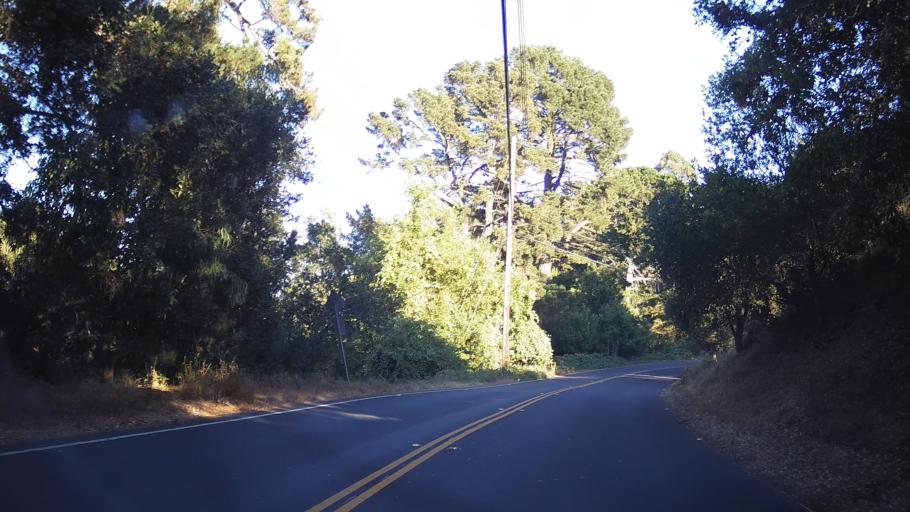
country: US
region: California
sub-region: Contra Costa County
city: Orinda
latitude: 37.8486
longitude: -122.2012
